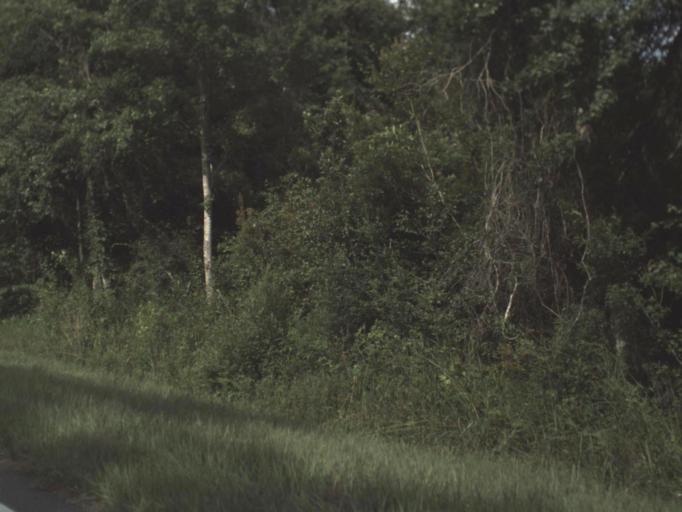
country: US
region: Florida
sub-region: Madison County
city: Madison
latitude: 30.3926
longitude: -83.6562
